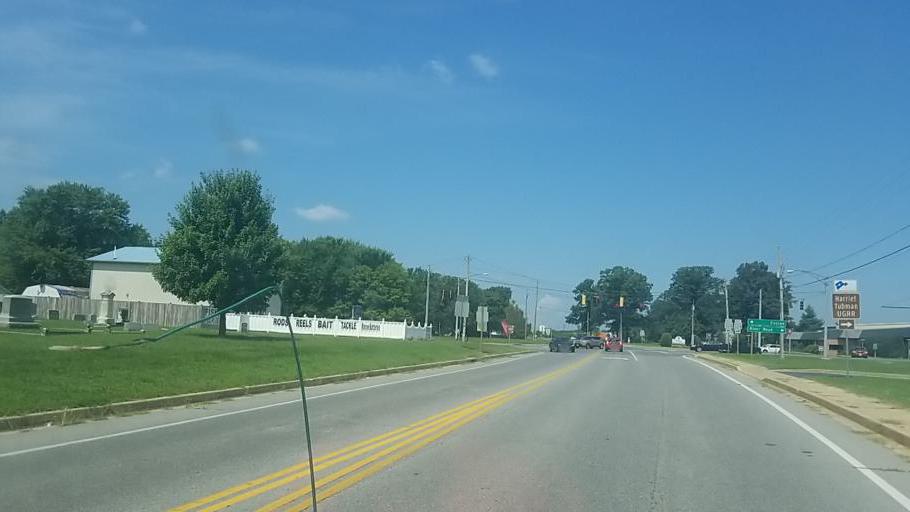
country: US
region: Maryland
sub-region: Caroline County
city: Denton
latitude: 38.8906
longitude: -75.8413
